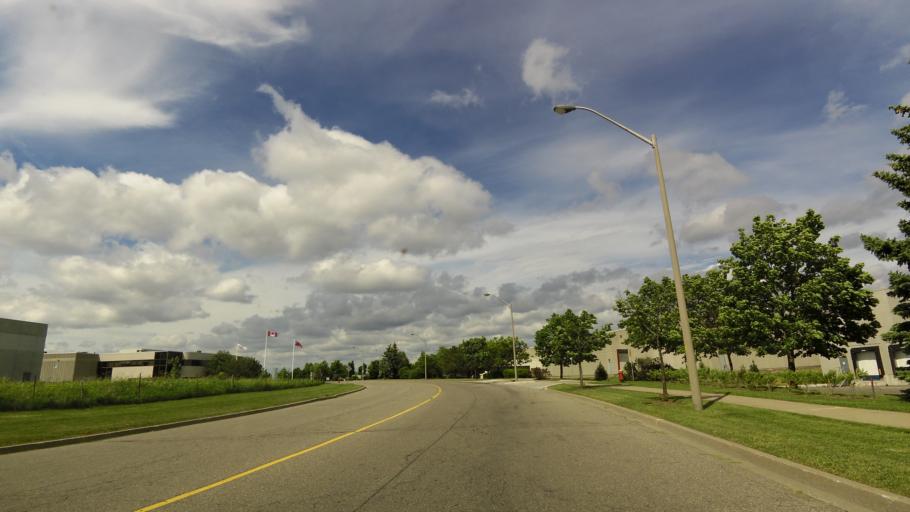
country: CA
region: Ontario
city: Oakville
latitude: 43.5104
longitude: -79.6748
